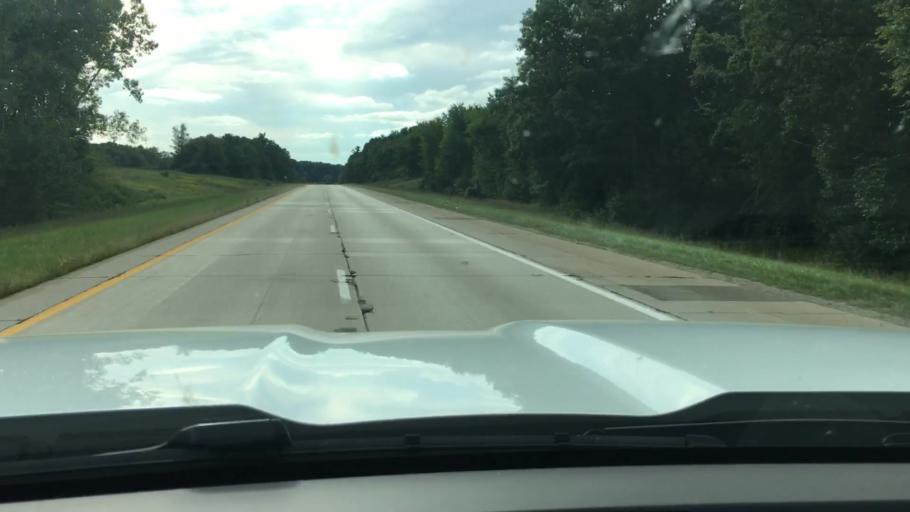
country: US
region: Michigan
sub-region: Lapeer County
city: Imlay City
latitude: 43.0092
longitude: -83.2007
